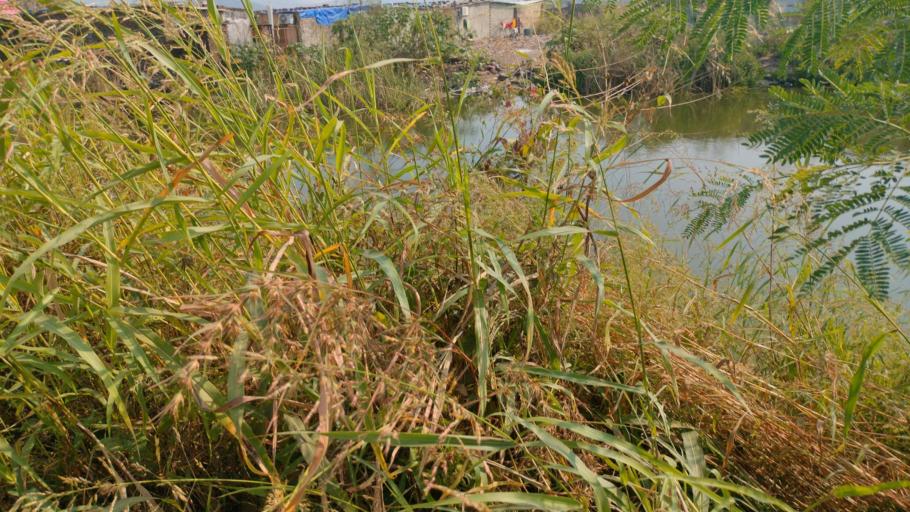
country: IN
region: Maharashtra
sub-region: Thane
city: Bhayandar
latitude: 19.3549
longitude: 72.8646
